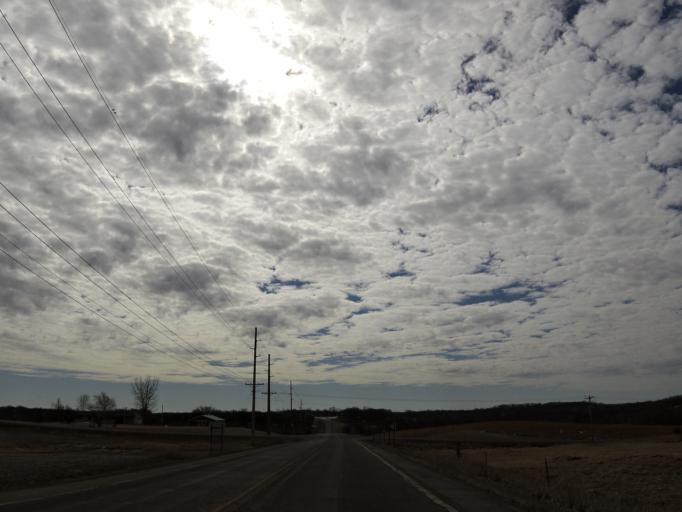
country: US
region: Minnesota
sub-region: Scott County
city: Jordan
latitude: 44.6317
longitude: -93.5628
